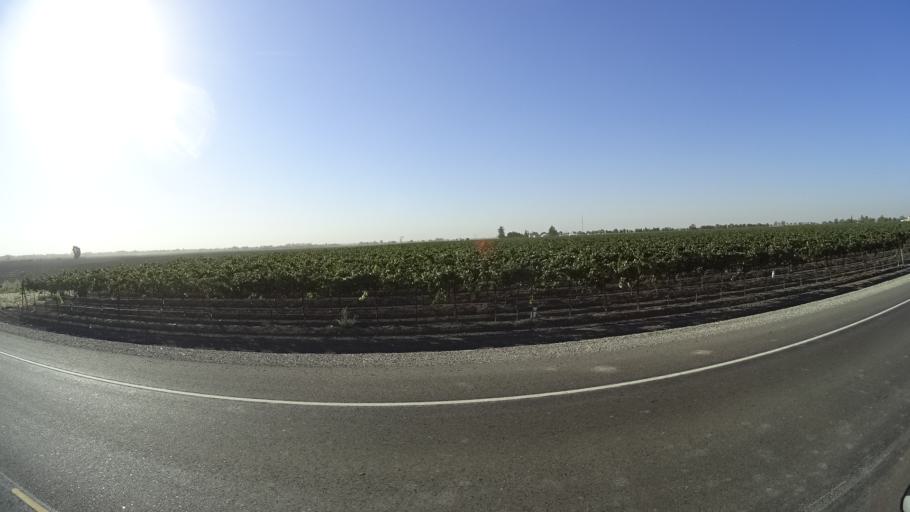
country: US
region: California
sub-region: Sacramento County
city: Parkway
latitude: 38.4147
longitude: -121.5739
